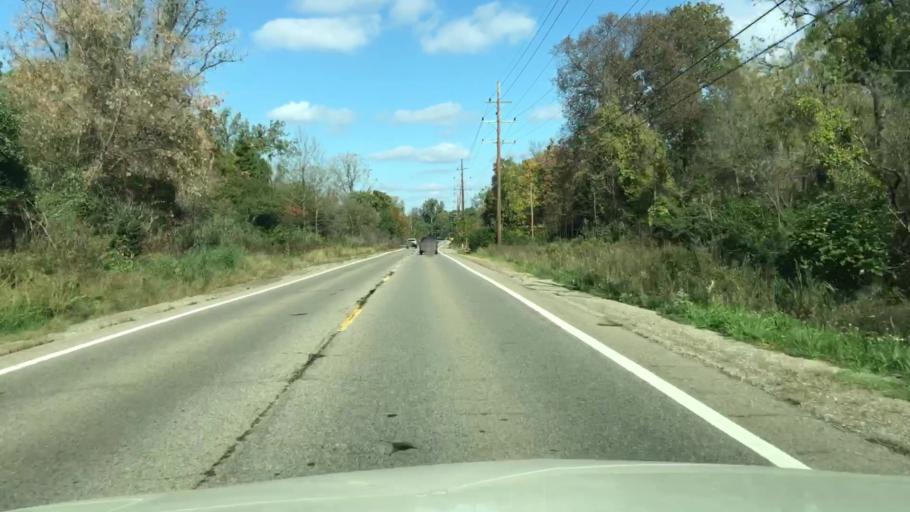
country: US
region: Michigan
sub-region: Oakland County
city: Rochester
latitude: 42.6632
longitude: -83.0933
